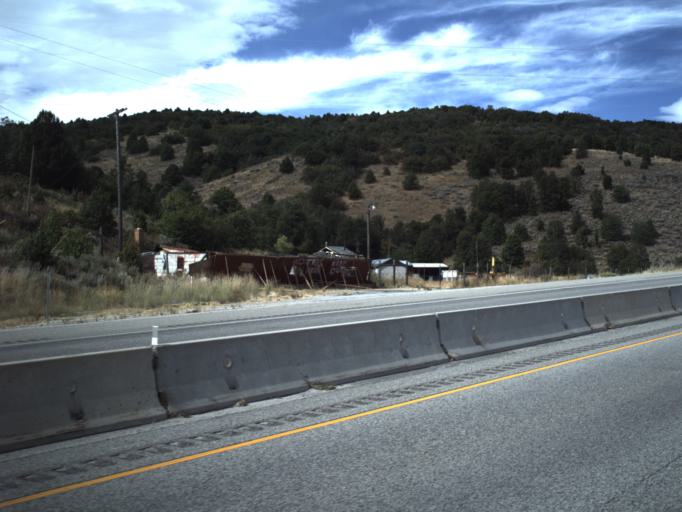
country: US
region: Utah
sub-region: Box Elder County
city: Brigham City
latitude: 41.5375
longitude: -111.9580
